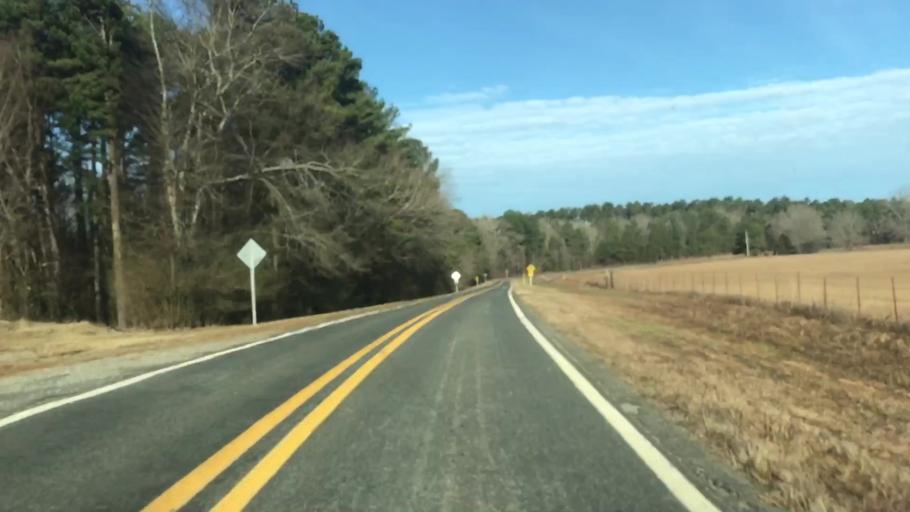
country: US
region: Arkansas
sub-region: Garland County
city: Rockwell
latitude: 34.4791
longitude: -93.2706
